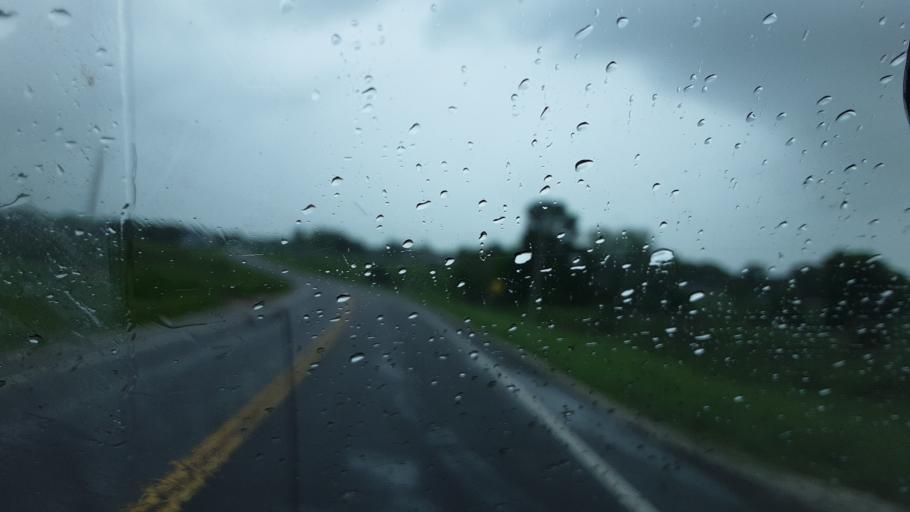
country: US
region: Missouri
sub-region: Monroe County
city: Paris
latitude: 39.4761
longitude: -92.1991
